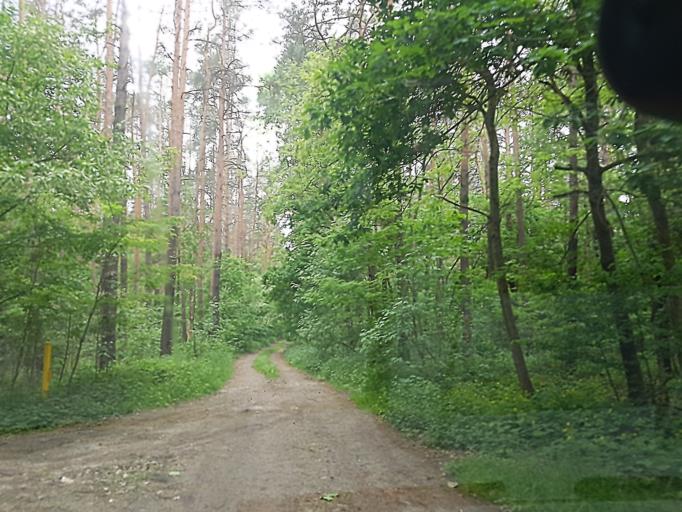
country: DE
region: Brandenburg
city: Finsterwalde
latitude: 51.5976
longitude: 13.7218
